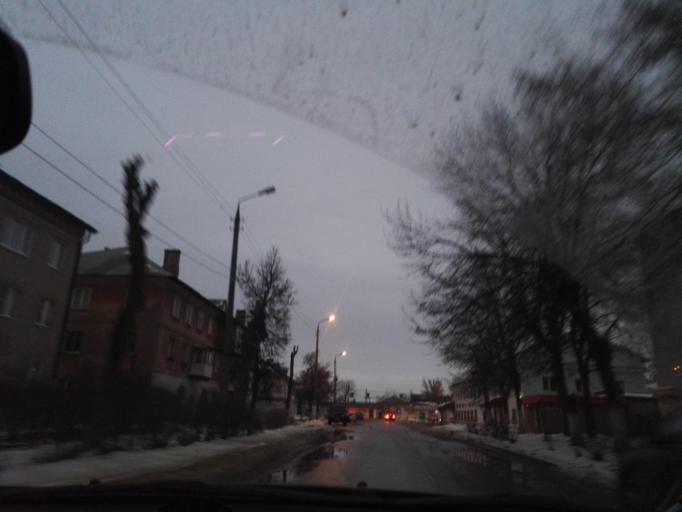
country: RU
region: Tula
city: Novomoskovsk
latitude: 54.0059
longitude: 38.3003
